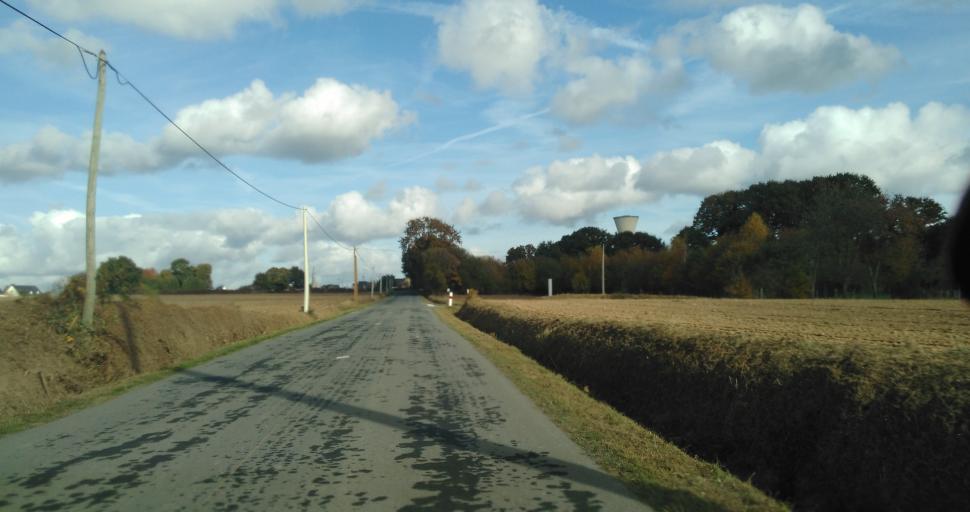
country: FR
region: Brittany
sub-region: Departement d'Ille-et-Vilaine
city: Boisgervilly
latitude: 48.1612
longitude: -2.0678
